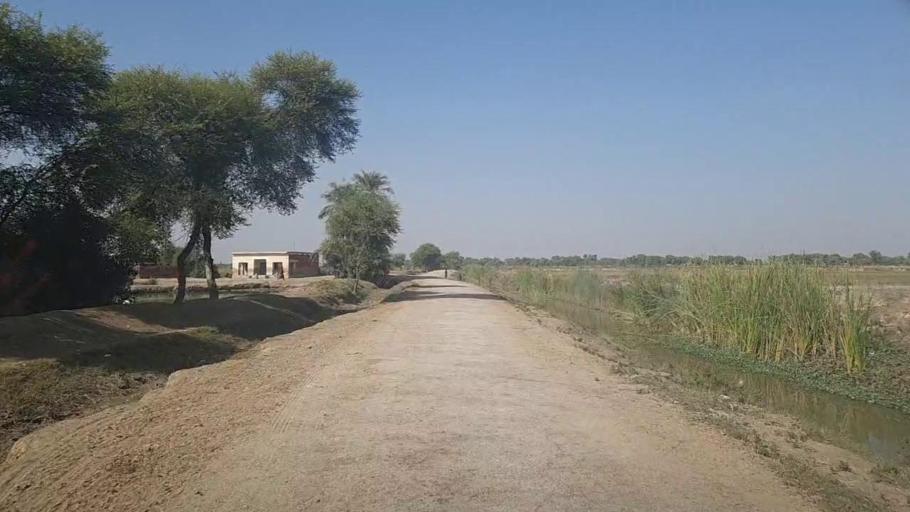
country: PK
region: Sindh
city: Thul
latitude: 28.3112
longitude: 68.7680
